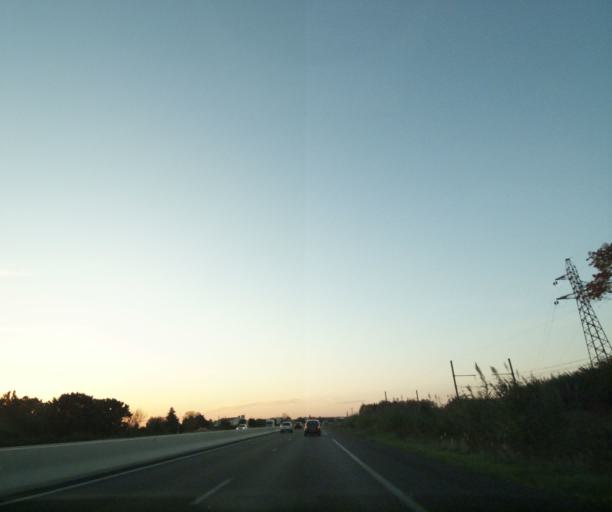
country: FR
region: Provence-Alpes-Cote d'Azur
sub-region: Departement des Bouches-du-Rhone
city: Arles
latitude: 43.6544
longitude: 4.6593
